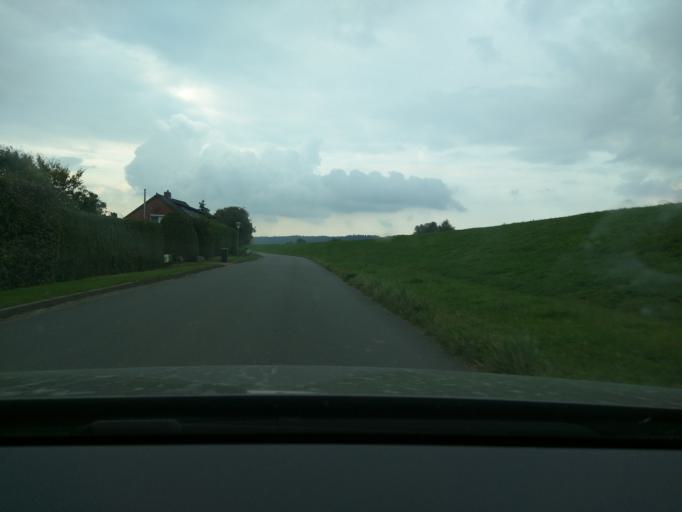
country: DE
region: Lower Saxony
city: Artlenburg
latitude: 53.3715
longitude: 10.4970
